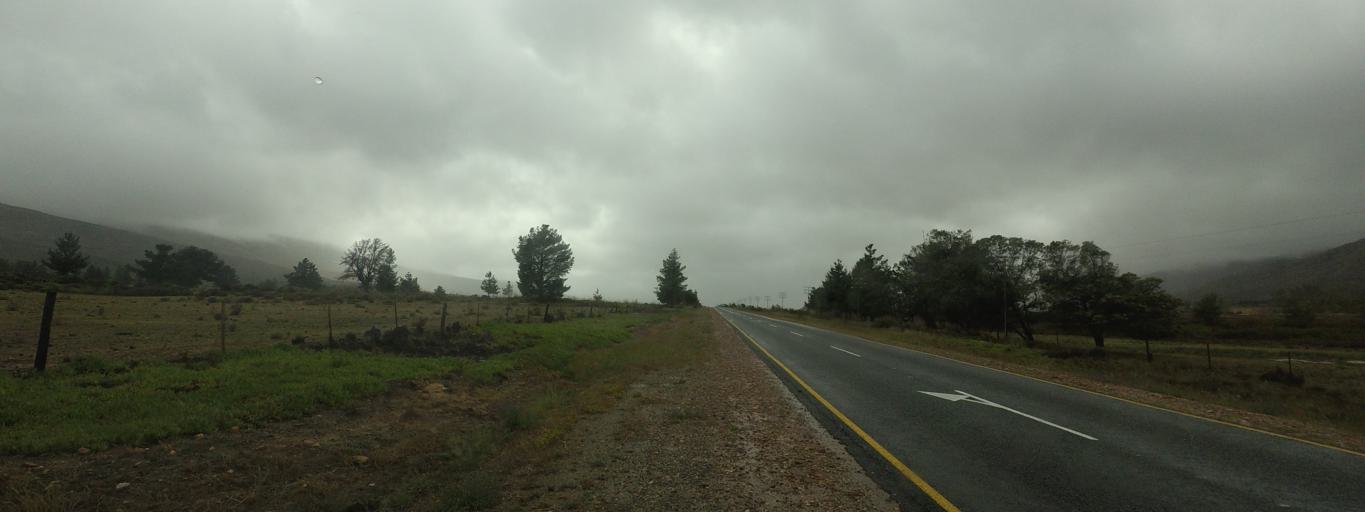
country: ZA
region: Western Cape
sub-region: Eden District Municipality
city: George
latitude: -33.8300
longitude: 22.4631
